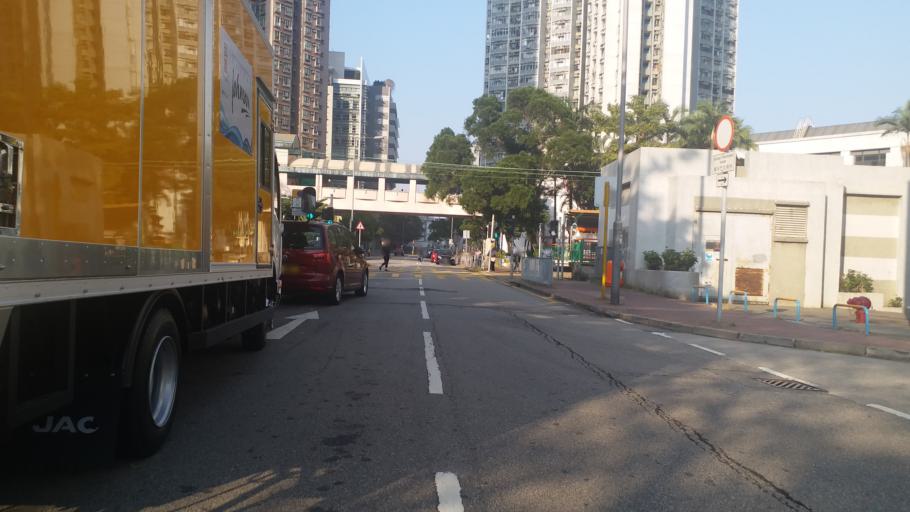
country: HK
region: Tuen Mun
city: Tuen Mun
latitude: 22.4064
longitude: 113.9688
